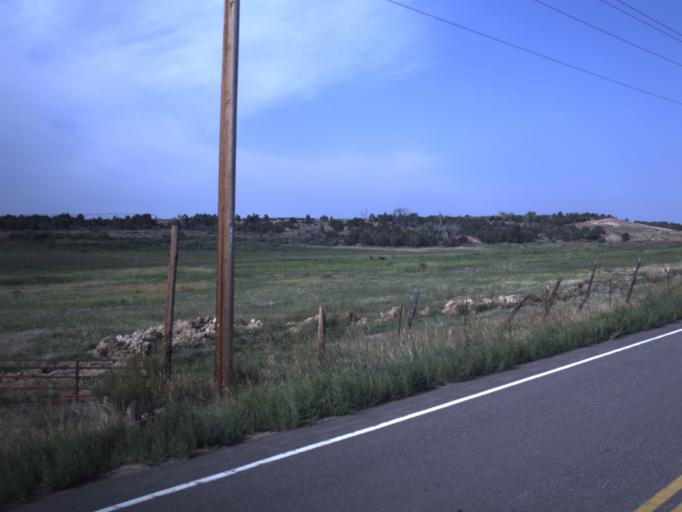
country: US
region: Utah
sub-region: Duchesne County
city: Duchesne
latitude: 40.3556
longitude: -110.3469
